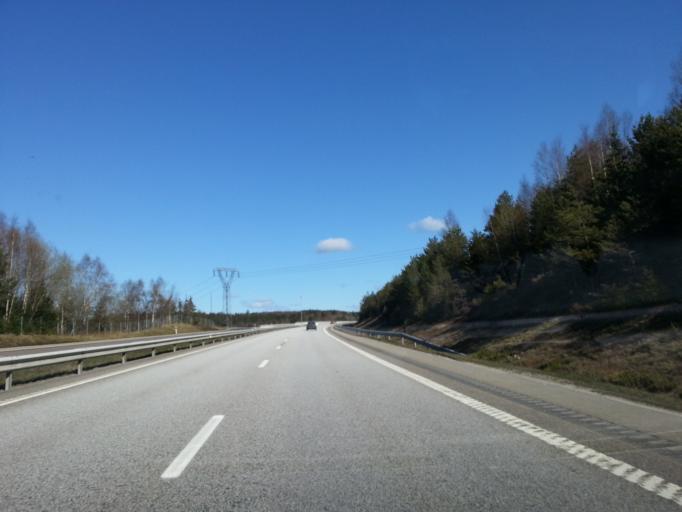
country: SE
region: Vaestra Goetaland
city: Svanesund
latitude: 58.1069
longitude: 11.8797
